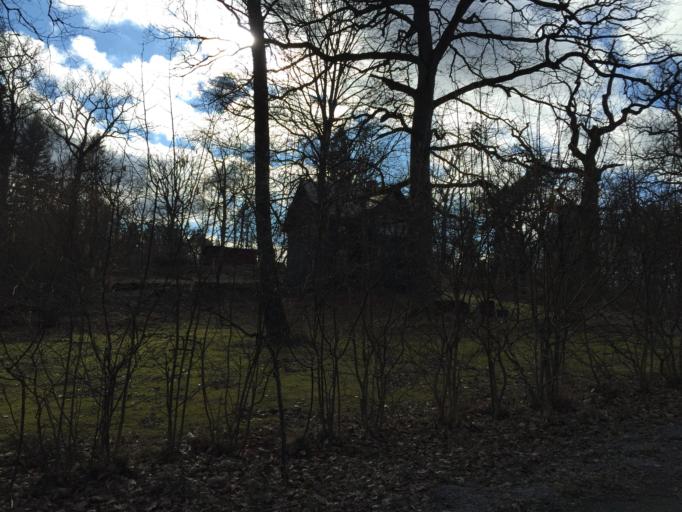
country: SE
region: Stockholm
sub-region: Salems Kommun
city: Ronninge
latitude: 59.1859
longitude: 17.7188
